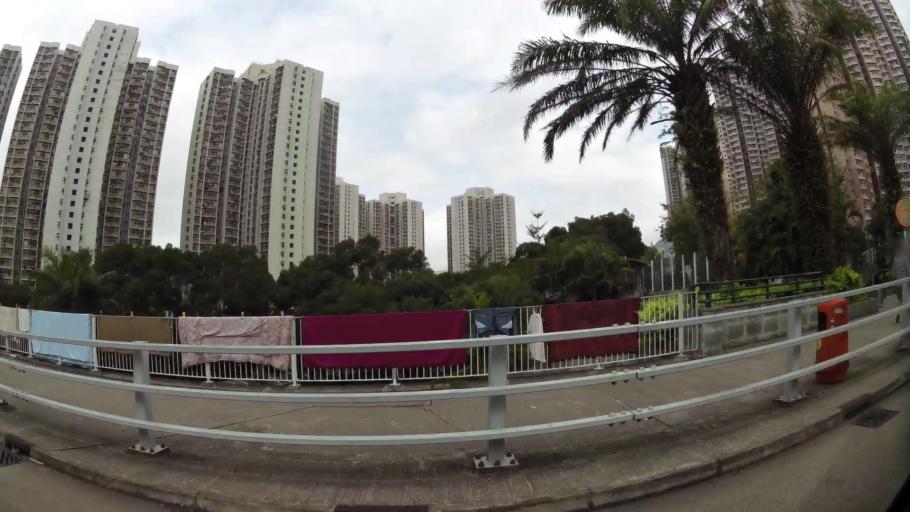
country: HK
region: Kowloon City
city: Kowloon
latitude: 22.3200
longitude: 114.2313
